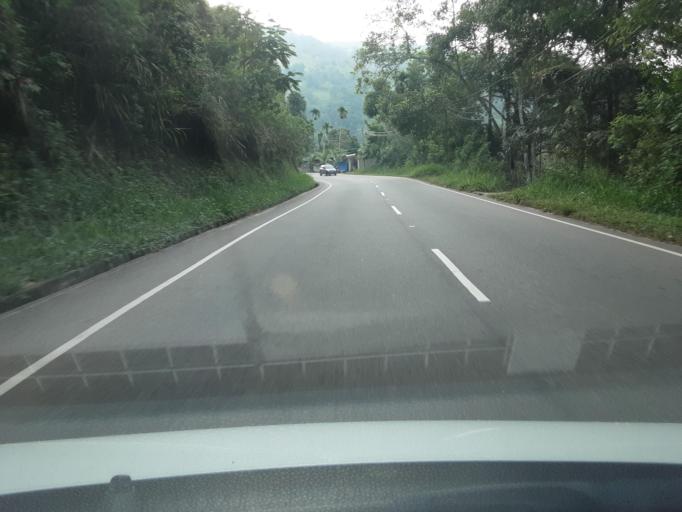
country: LK
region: Uva
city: Badulla
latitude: 6.9538
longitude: 81.0251
